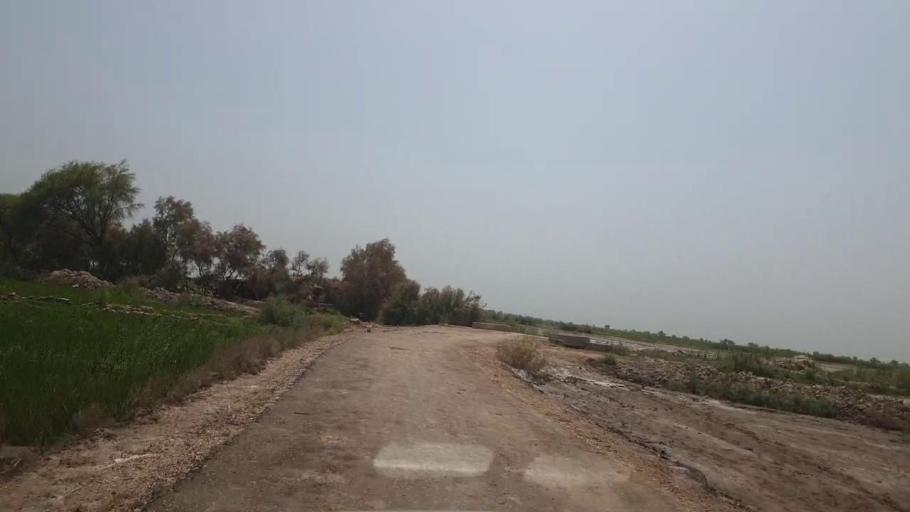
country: PK
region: Sindh
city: Garhi Yasin
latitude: 28.0565
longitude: 68.3161
